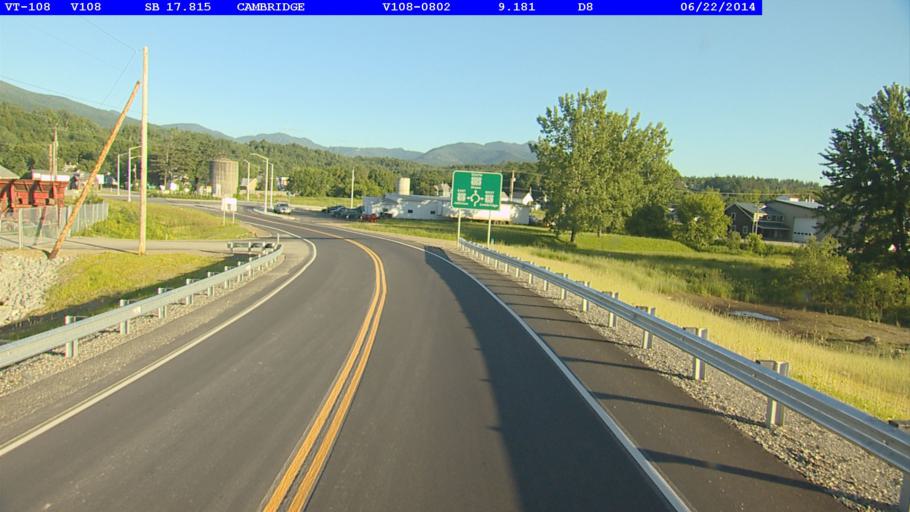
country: US
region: Vermont
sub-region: Lamoille County
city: Johnson
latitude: 44.6487
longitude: -72.8307
